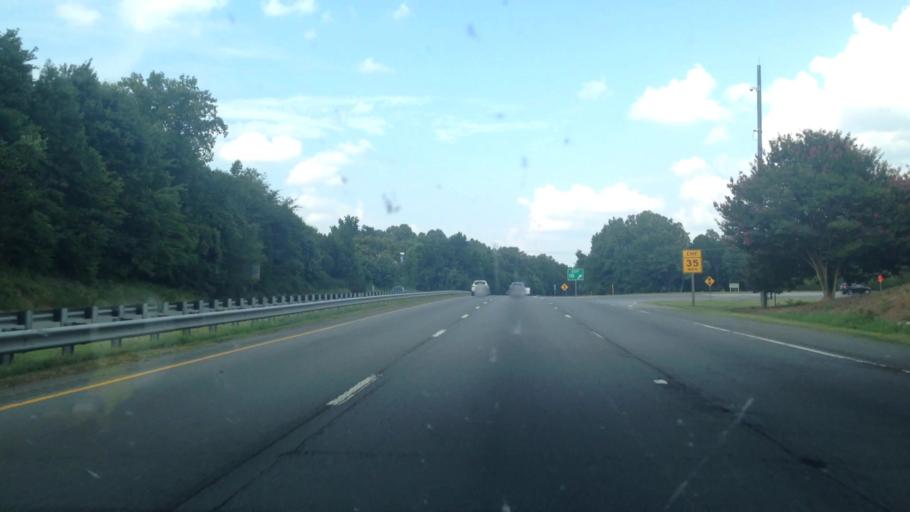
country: US
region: North Carolina
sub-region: Forsyth County
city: Walkertown
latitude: 36.1112
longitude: -80.1650
